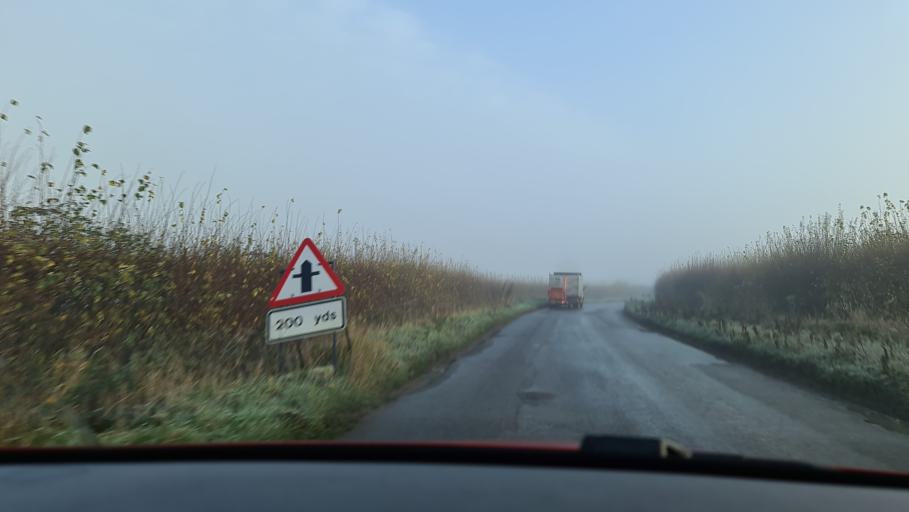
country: GB
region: England
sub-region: Buckinghamshire
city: Aylesbury
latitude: 51.7819
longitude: -0.8032
